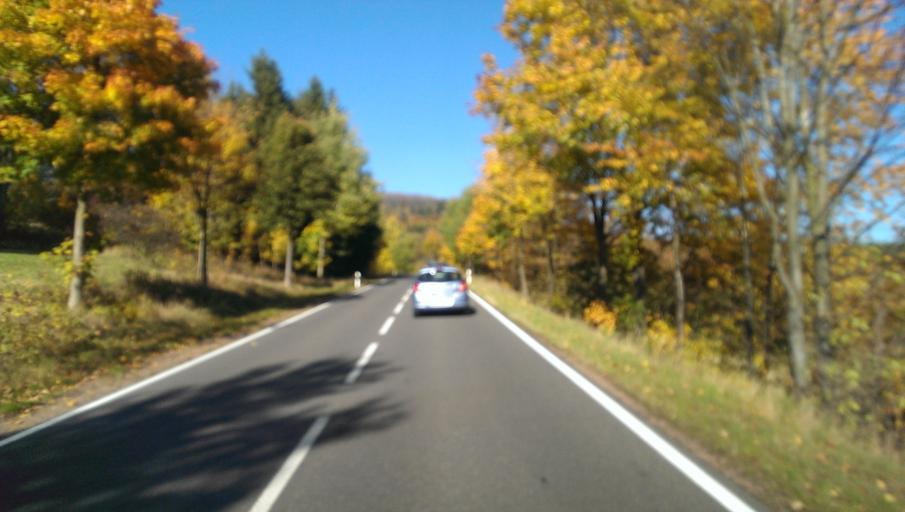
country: DE
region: Saxony
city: Geising
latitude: 50.7638
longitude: 13.7795
